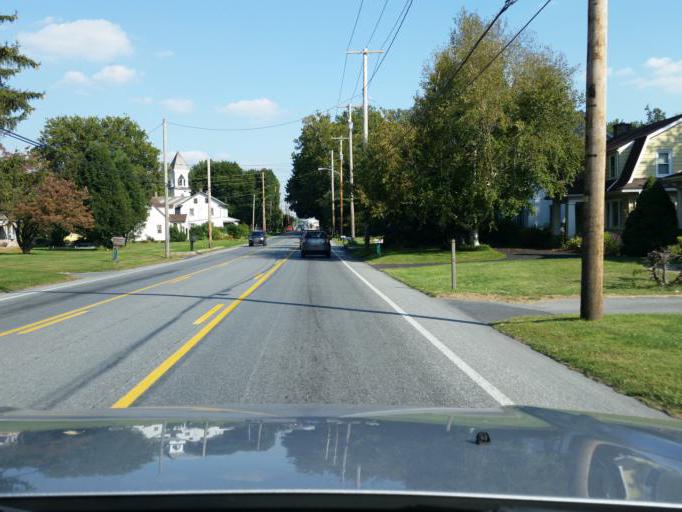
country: US
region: Pennsylvania
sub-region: Lancaster County
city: Paradise
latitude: 40.0088
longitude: -76.1240
